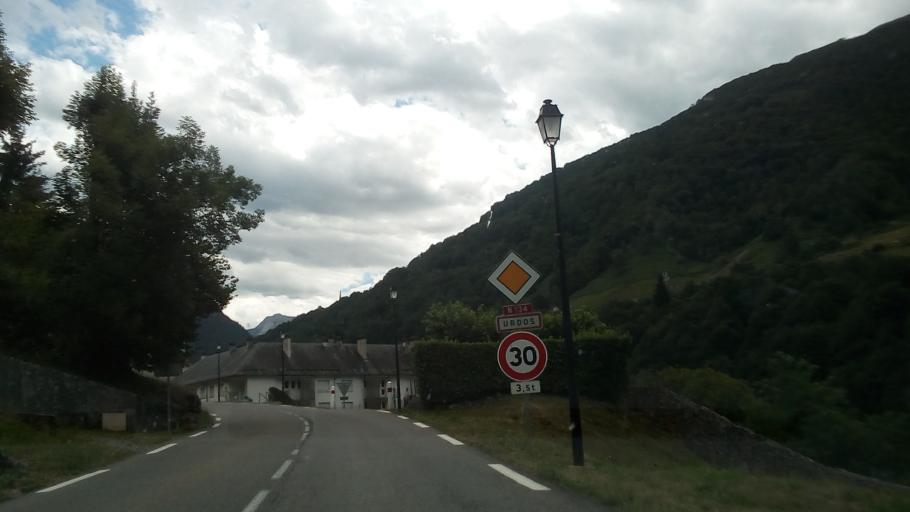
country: ES
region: Aragon
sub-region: Provincia de Huesca
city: Canfranc
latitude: 42.8747
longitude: -0.5550
